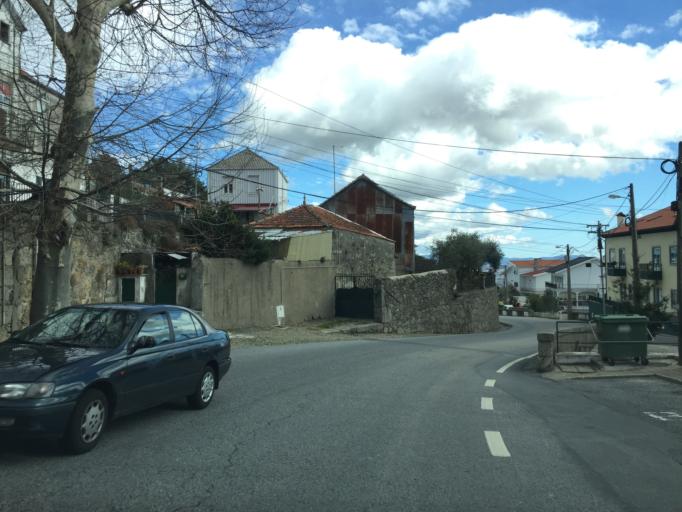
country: PT
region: Castelo Branco
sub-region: Covilha
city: Covilha
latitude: 40.2811
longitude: -7.5125
